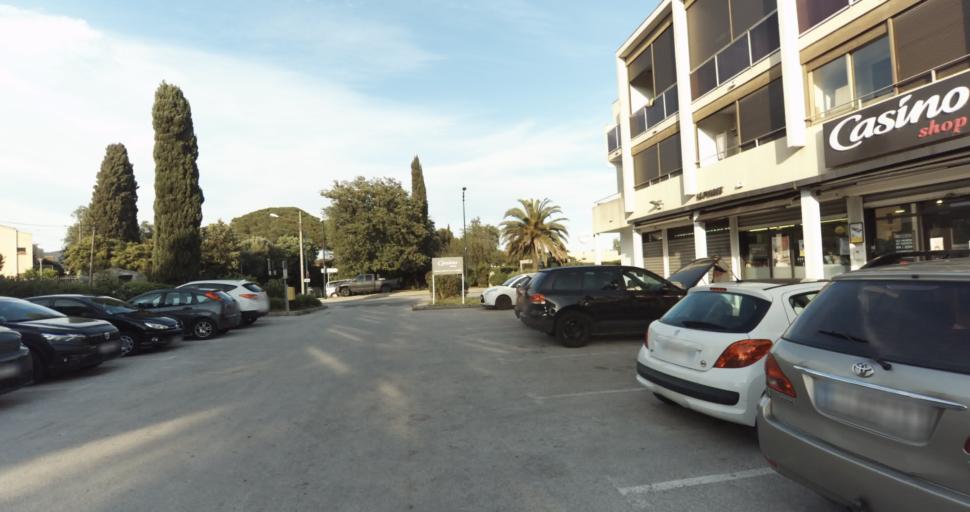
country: FR
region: Provence-Alpes-Cote d'Azur
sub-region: Departement du Var
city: Hyeres
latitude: 43.1245
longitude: 6.1508
